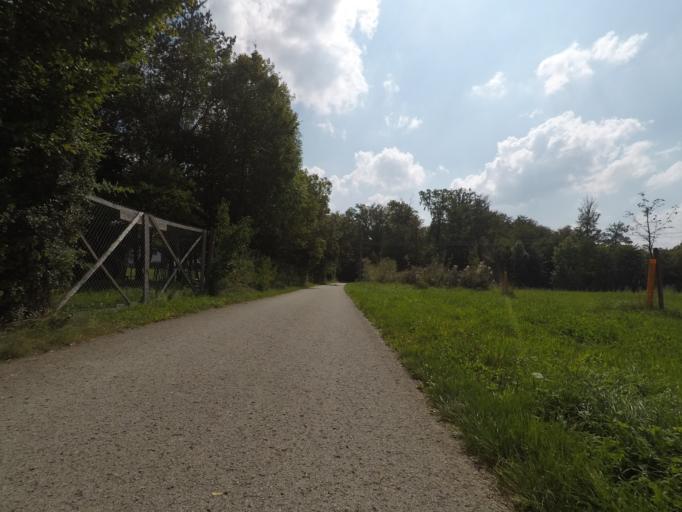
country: DE
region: Baden-Wuerttemberg
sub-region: Regierungsbezirk Stuttgart
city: Altbach
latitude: 48.7506
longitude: 9.3802
